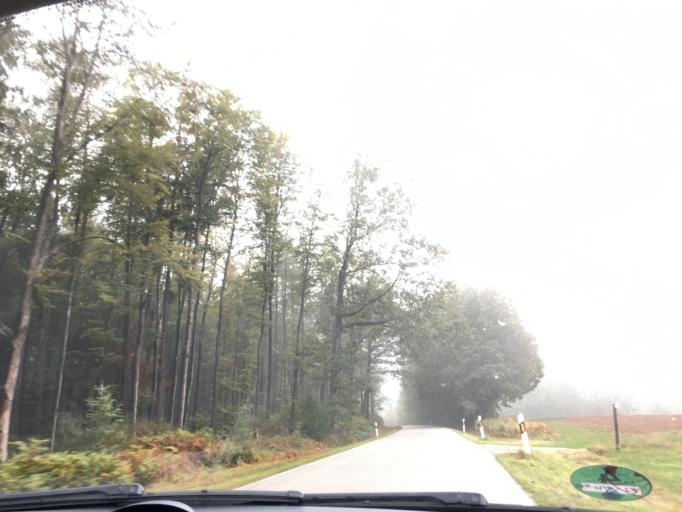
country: DE
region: Rheinland-Pfalz
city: Schmalenberg
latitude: 49.3211
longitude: 7.7584
